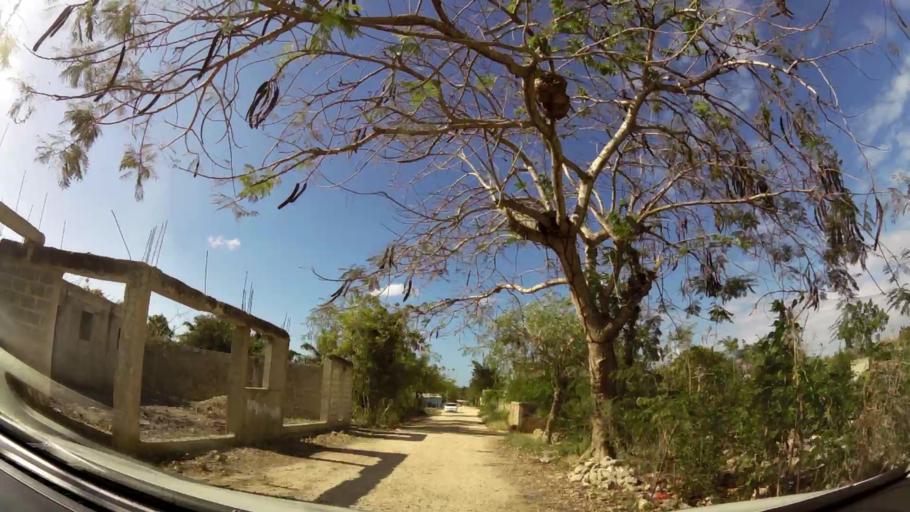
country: DO
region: Santo Domingo
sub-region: Santo Domingo
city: Boca Chica
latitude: 18.4629
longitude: -69.6016
